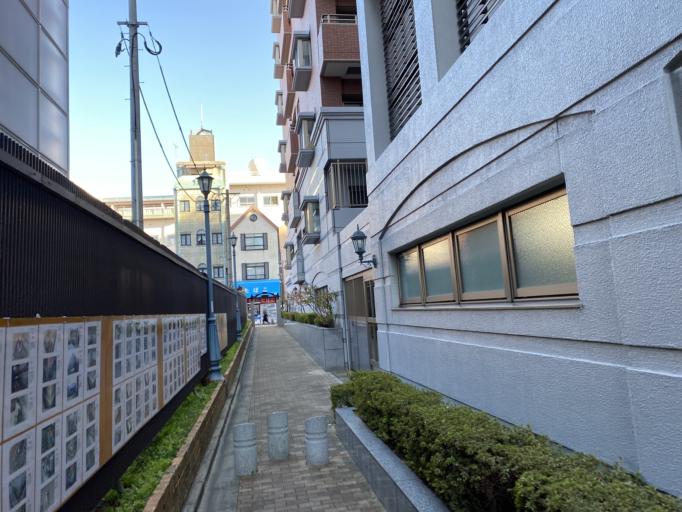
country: JP
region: Nagasaki
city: Nagasaki-shi
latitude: 32.7384
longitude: 129.8715
